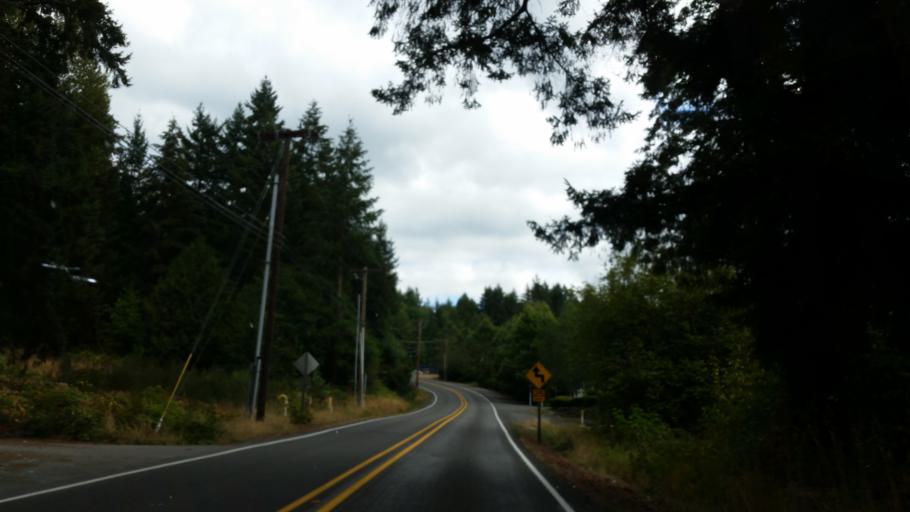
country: US
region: Washington
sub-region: Pierce County
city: Sumner
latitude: 47.2318
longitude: -122.2107
